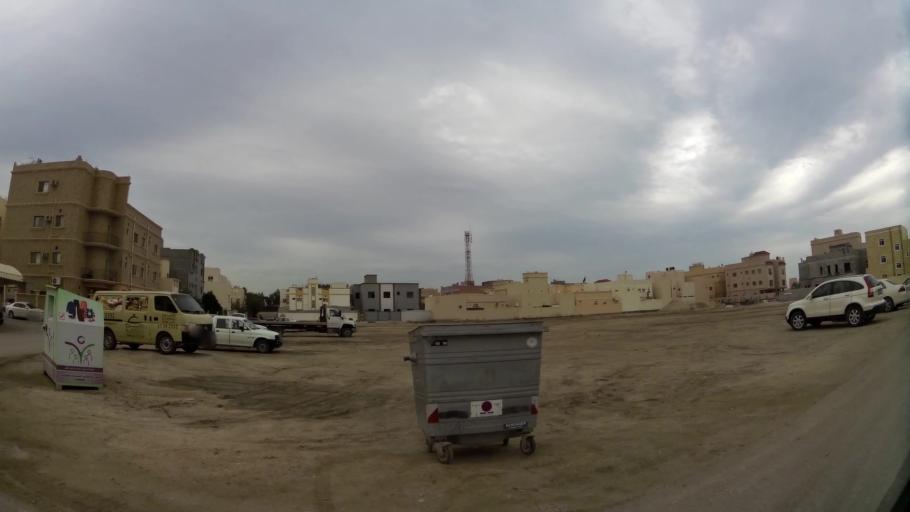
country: BH
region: Northern
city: Sitrah
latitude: 26.1702
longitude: 50.6059
